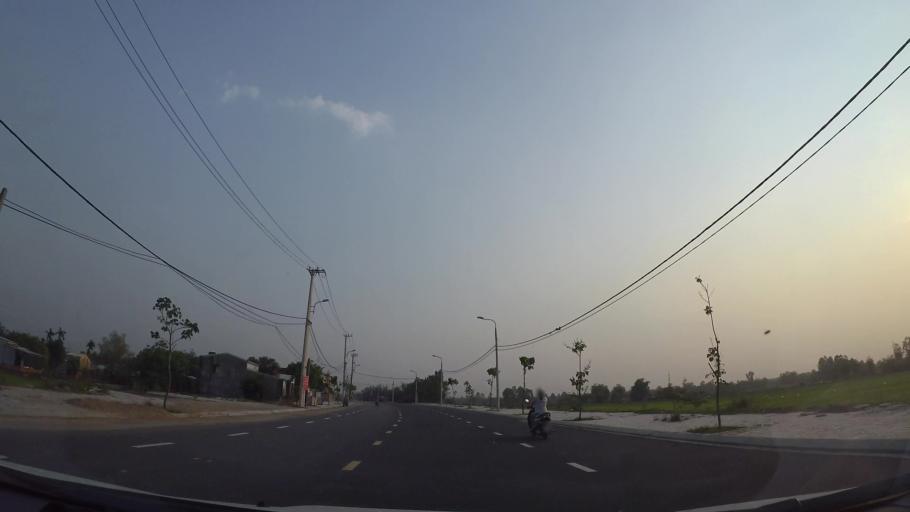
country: VN
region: Da Nang
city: Ngu Hanh Son
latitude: 15.9646
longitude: 108.2312
